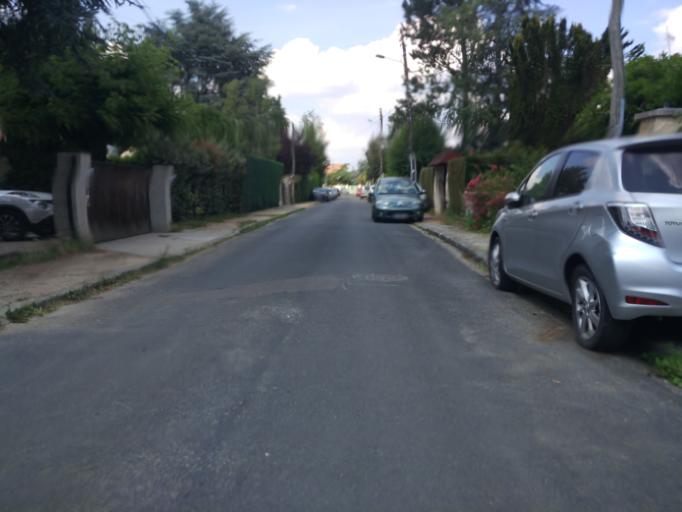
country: FR
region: Ile-de-France
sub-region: Departement des Yvelines
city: Saint-Remy-les-Chevreuse
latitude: 48.6962
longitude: 2.0600
